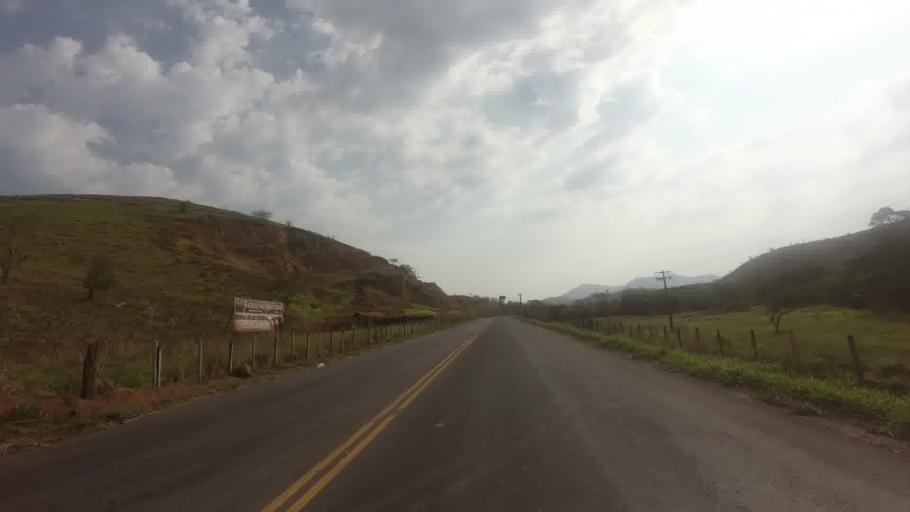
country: BR
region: Rio de Janeiro
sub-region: Itaperuna
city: Itaperuna
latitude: -21.3624
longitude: -41.9271
